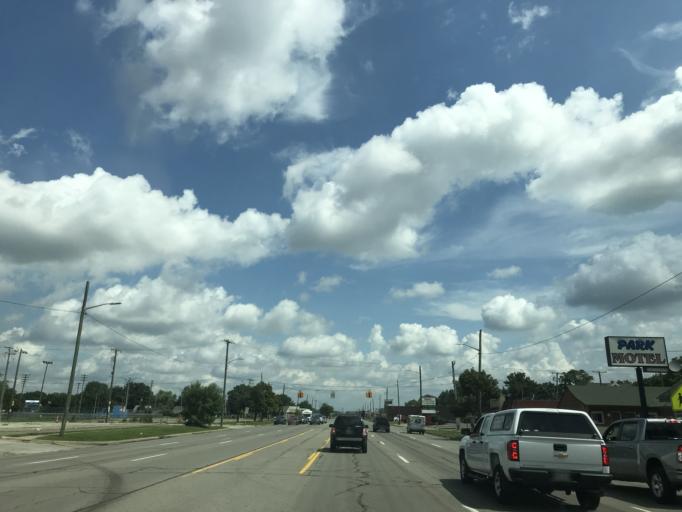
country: US
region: Michigan
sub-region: Wayne County
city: Lincoln Park
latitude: 42.2575
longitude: -83.1912
